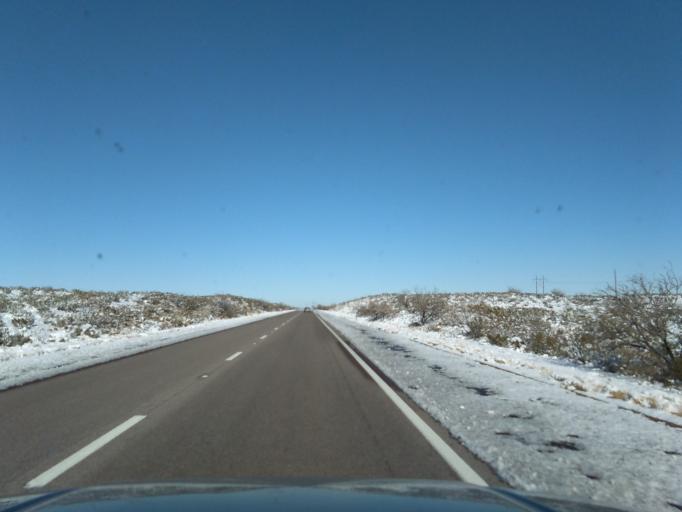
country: US
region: New Mexico
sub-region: Socorro County
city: Socorro
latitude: 33.6730
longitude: -107.0784
